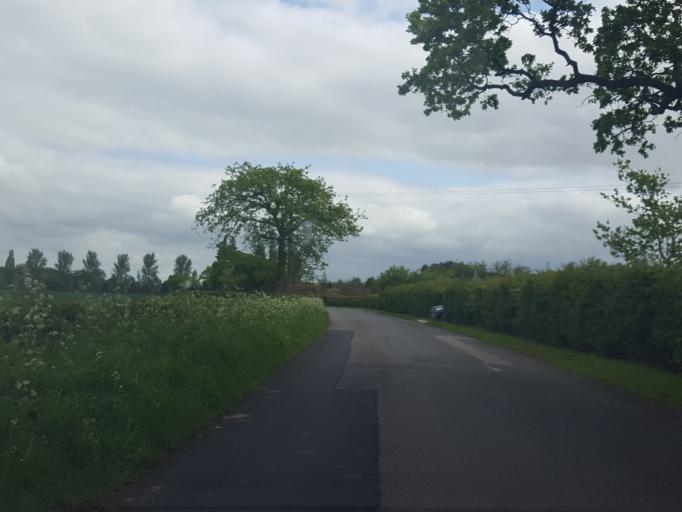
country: GB
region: England
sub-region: Essex
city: Little Clacton
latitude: 51.8248
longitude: 1.1116
